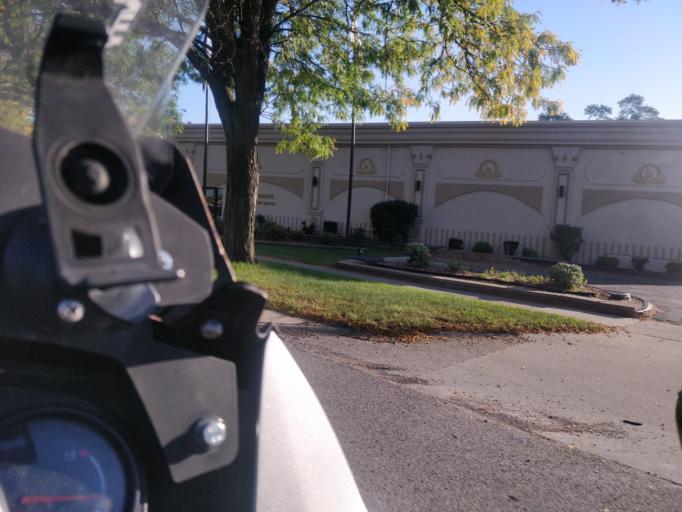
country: US
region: Michigan
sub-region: Wayne County
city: Melvindale
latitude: 42.2684
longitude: -83.1787
